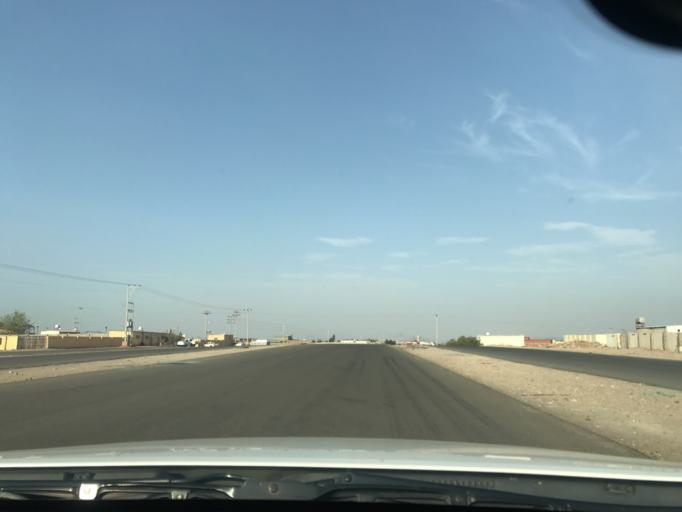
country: SA
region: Makkah
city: Al Jumum
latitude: 21.4531
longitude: 39.5327
